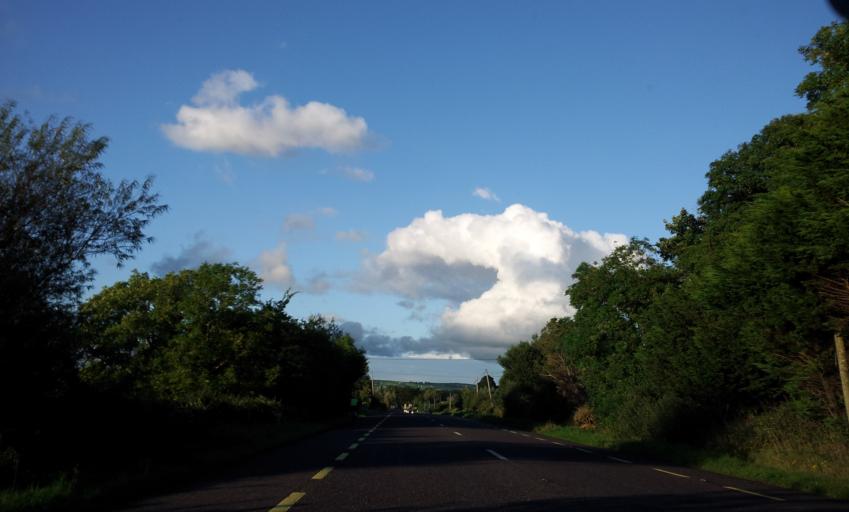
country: IE
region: Munster
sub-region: County Limerick
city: Abbeyfeale
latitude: 52.3691
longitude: -9.3191
